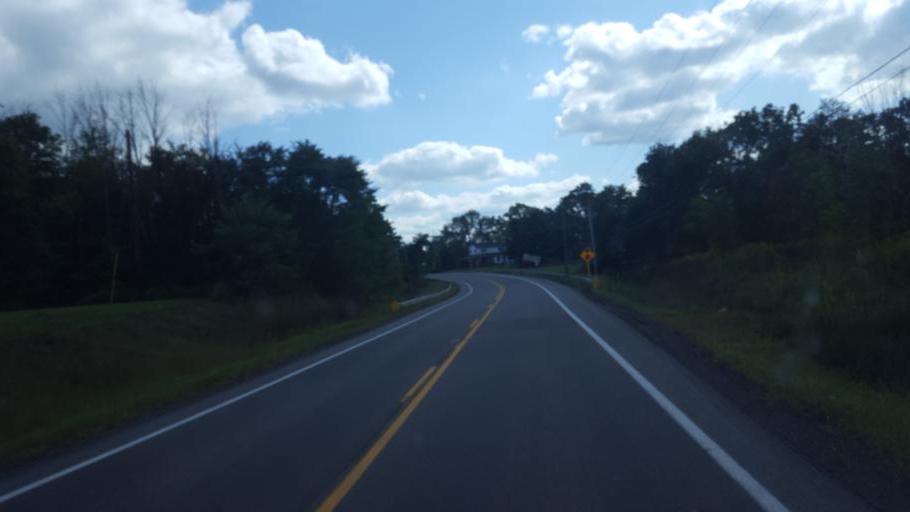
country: US
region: Ohio
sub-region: Ashland County
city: Ashland
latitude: 40.9039
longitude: -82.2142
